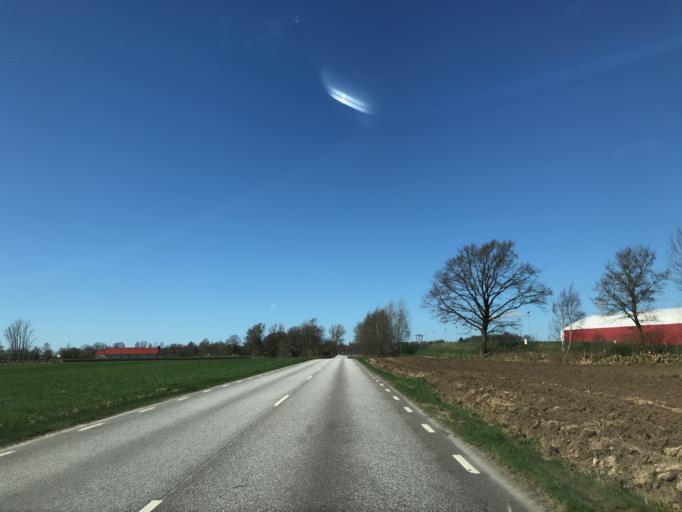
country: SE
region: Skane
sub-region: Klippans Kommun
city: Ljungbyhed
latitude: 56.0621
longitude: 13.2309
